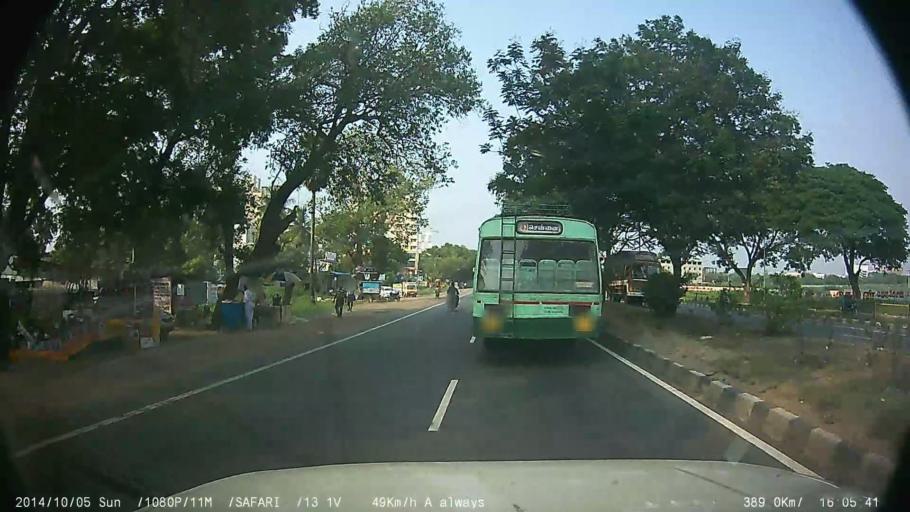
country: IN
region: Tamil Nadu
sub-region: Kancheepuram
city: Vandalur
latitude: 12.8710
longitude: 80.0769
